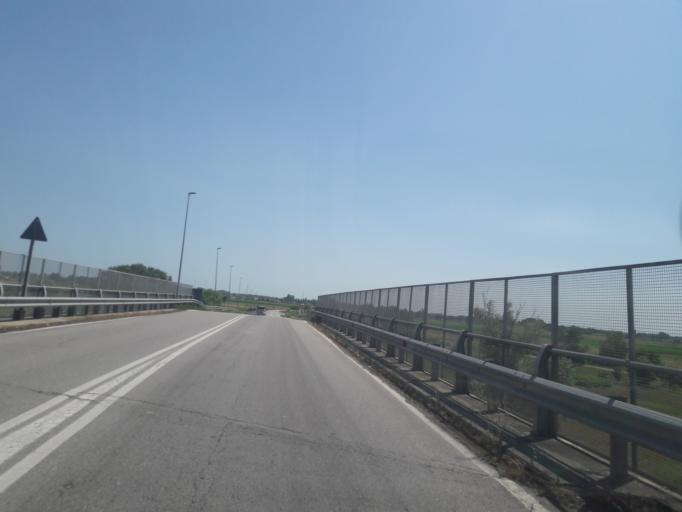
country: IT
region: Veneto
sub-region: Provincia di Rovigo
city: Corbola
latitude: 45.0095
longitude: 12.0973
